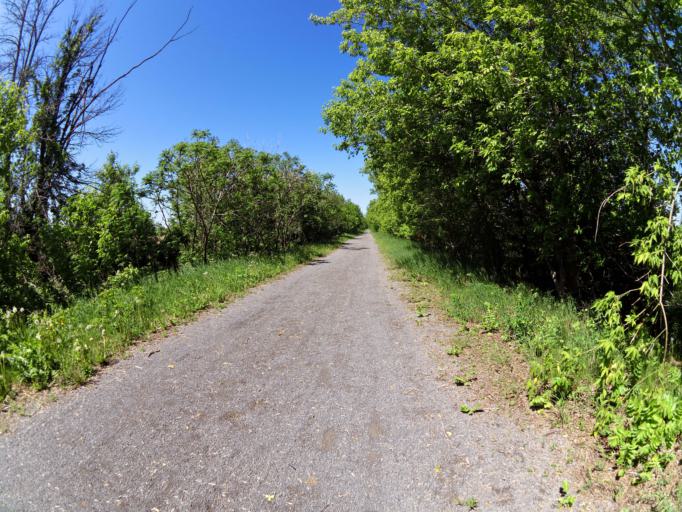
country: CA
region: Ontario
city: Clarence-Rockland
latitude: 45.4252
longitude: -75.3257
